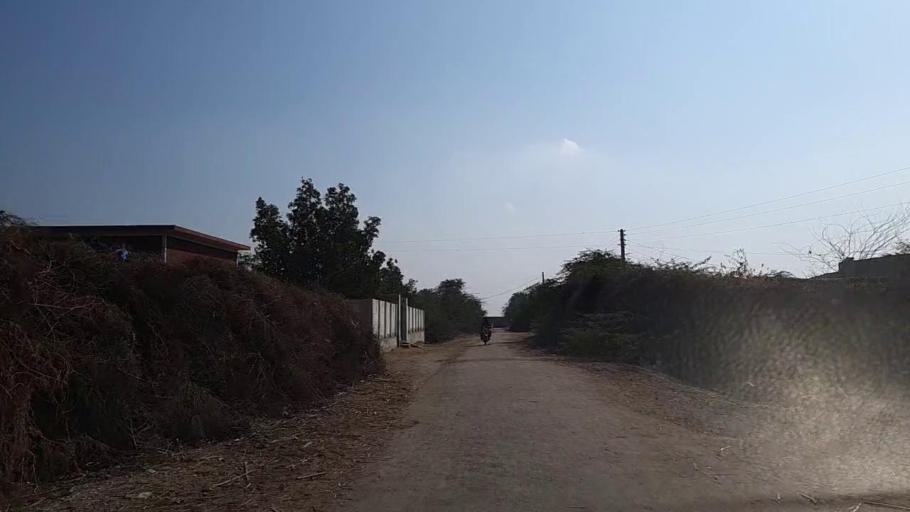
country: PK
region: Sindh
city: Jam Sahib
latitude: 26.2742
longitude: 68.5841
